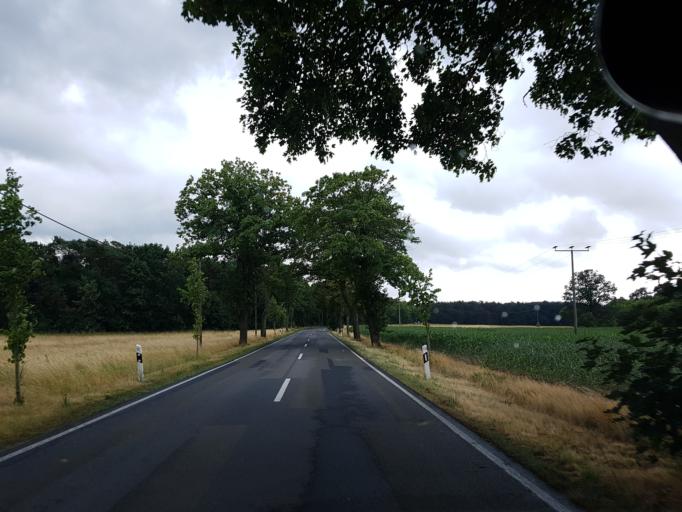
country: DE
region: Saxony-Anhalt
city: Seyda
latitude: 51.8965
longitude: 12.9354
